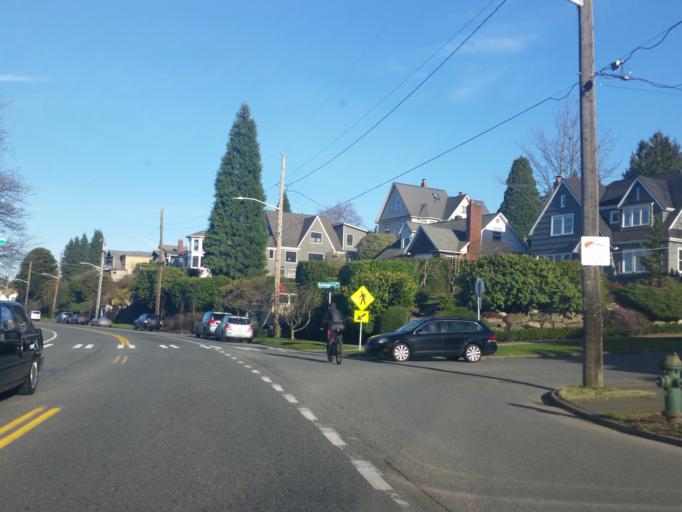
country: US
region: Washington
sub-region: King County
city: Seattle
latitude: 47.6720
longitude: -122.3379
